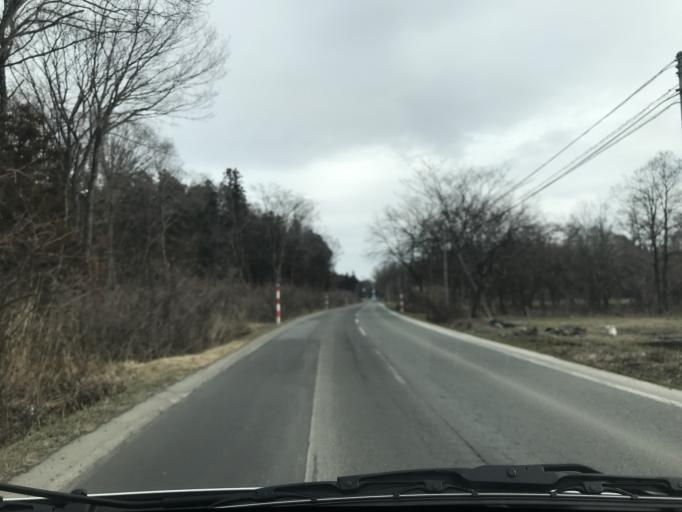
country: JP
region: Iwate
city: Kitakami
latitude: 39.3196
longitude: 141.0132
